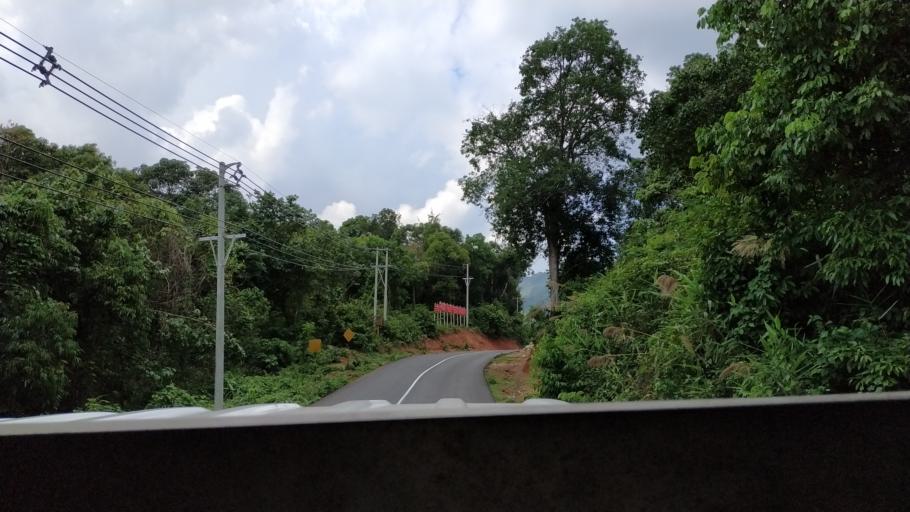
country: MM
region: Mon
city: Kyaikto
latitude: 17.4288
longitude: 97.0889
